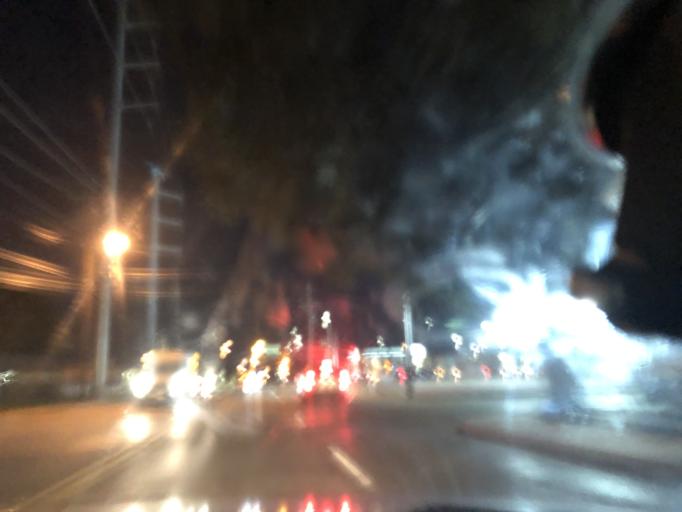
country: US
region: Texas
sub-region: Dallas County
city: University Park
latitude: 32.8274
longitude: -96.8437
